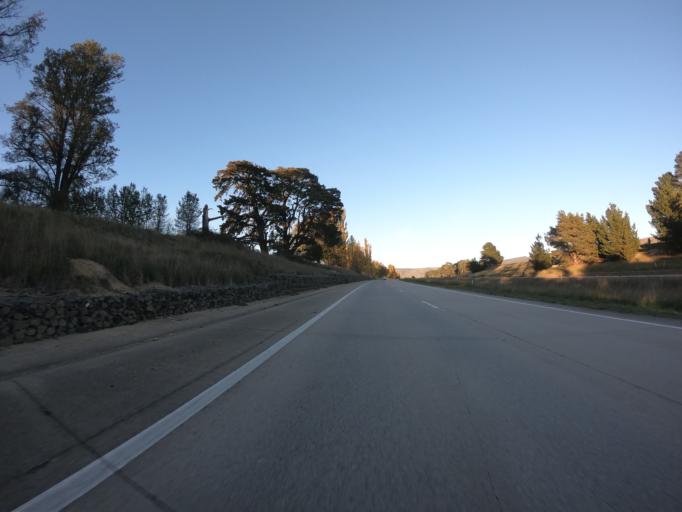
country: AU
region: New South Wales
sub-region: Yass Valley
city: Gundaroo
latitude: -34.9389
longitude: 149.4196
